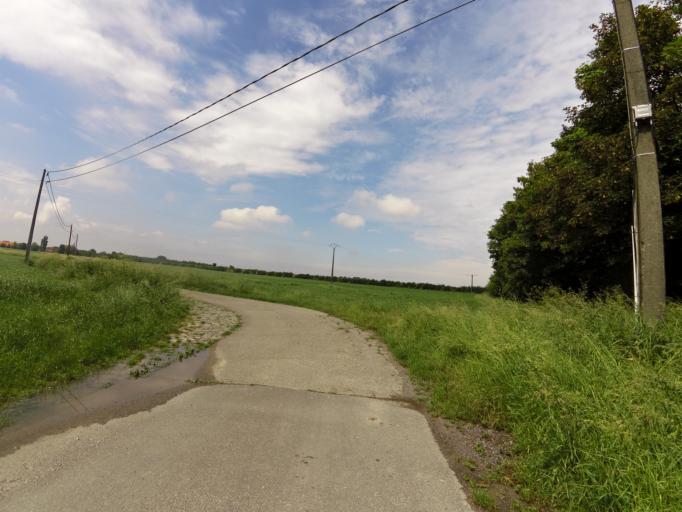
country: BE
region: Flanders
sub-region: Provincie West-Vlaanderen
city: Middelkerke
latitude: 51.1316
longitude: 2.8139
